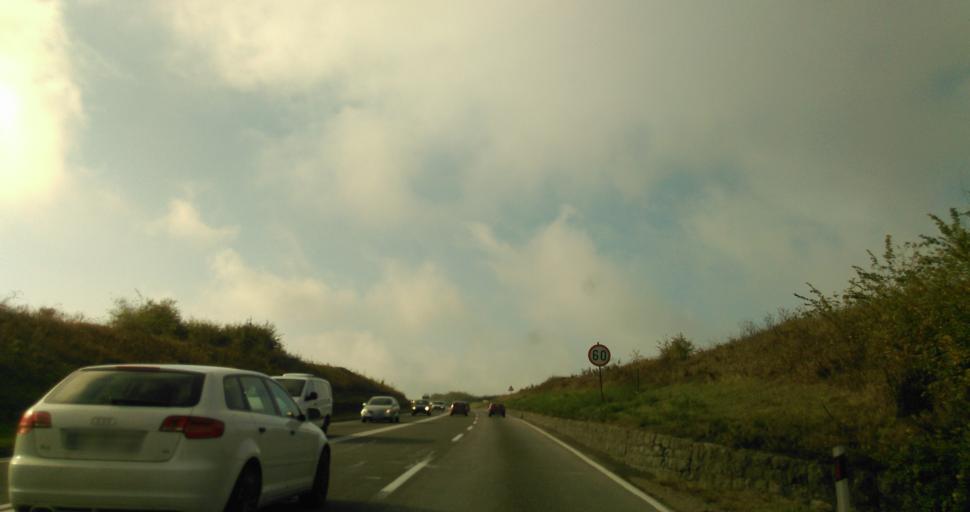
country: RS
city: Rusanj
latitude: 44.6768
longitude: 20.4279
